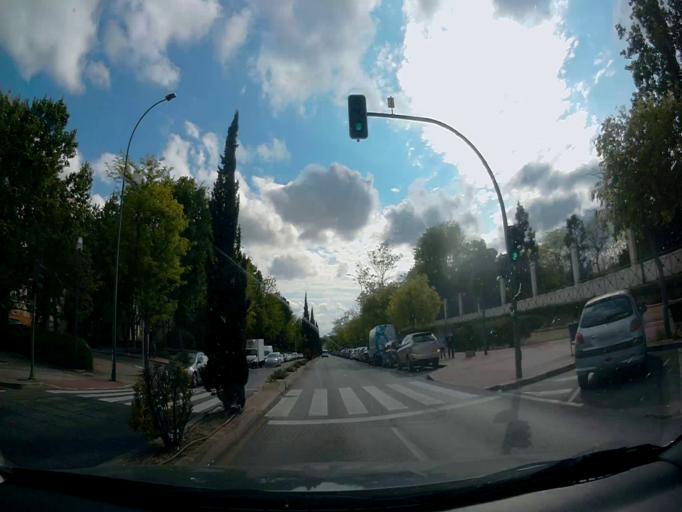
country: ES
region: Madrid
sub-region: Provincia de Madrid
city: Mostoles
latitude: 40.3228
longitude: -3.8728
